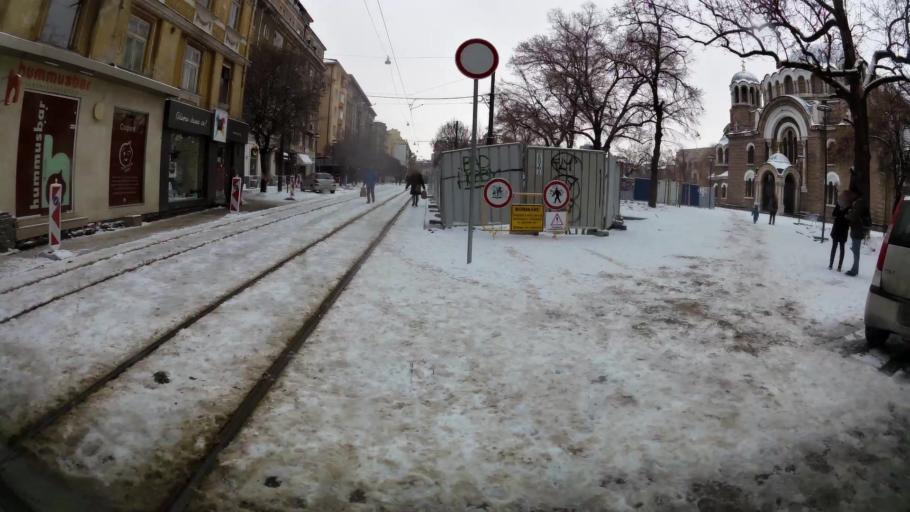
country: BG
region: Sofia-Capital
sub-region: Stolichna Obshtina
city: Sofia
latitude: 42.6894
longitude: 23.3275
